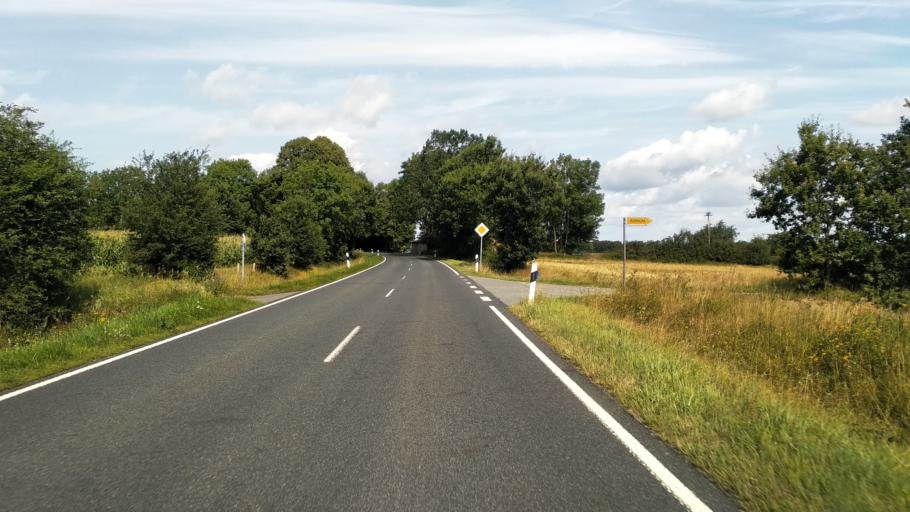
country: DE
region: Schleswig-Holstein
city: Lottorf
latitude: 54.4563
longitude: 9.5870
